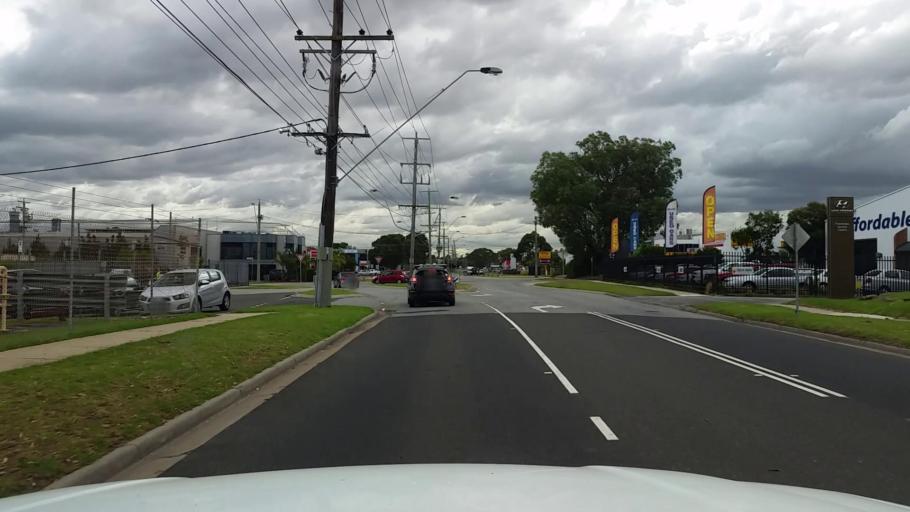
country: AU
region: Victoria
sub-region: Frankston
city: Frankston North
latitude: -38.1174
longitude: 145.1407
